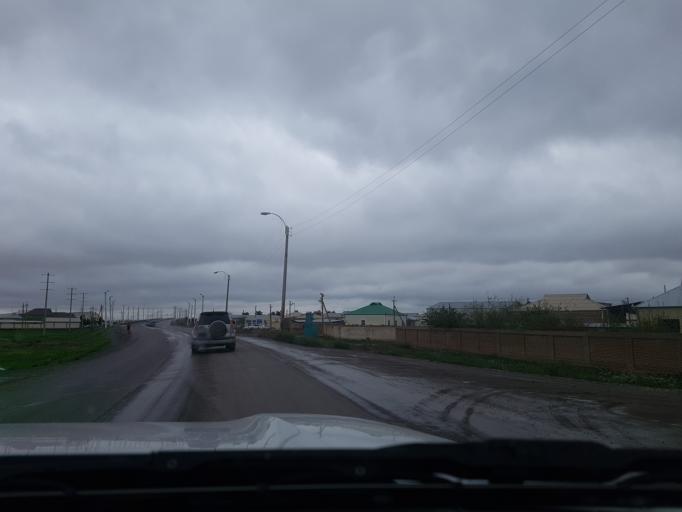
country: TM
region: Mary
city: Mary
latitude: 37.5864
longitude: 61.8815
